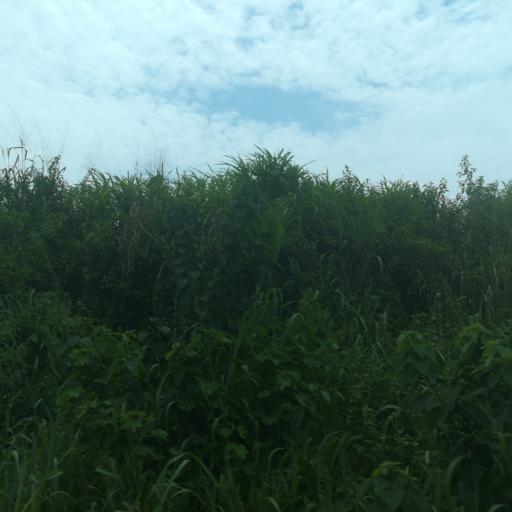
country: NG
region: Lagos
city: Ejirin
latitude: 6.6465
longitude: 3.7313
